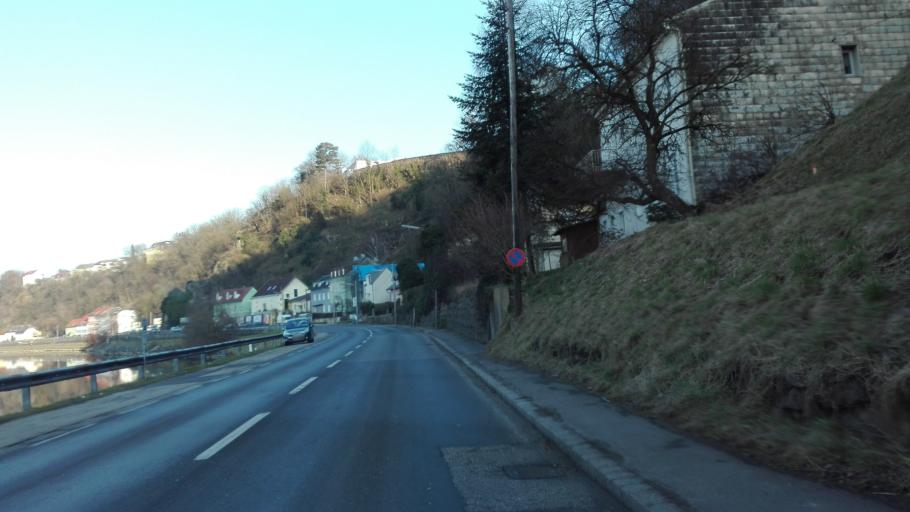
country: AT
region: Upper Austria
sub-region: Linz Stadt
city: Linz
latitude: 48.3041
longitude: 14.2698
